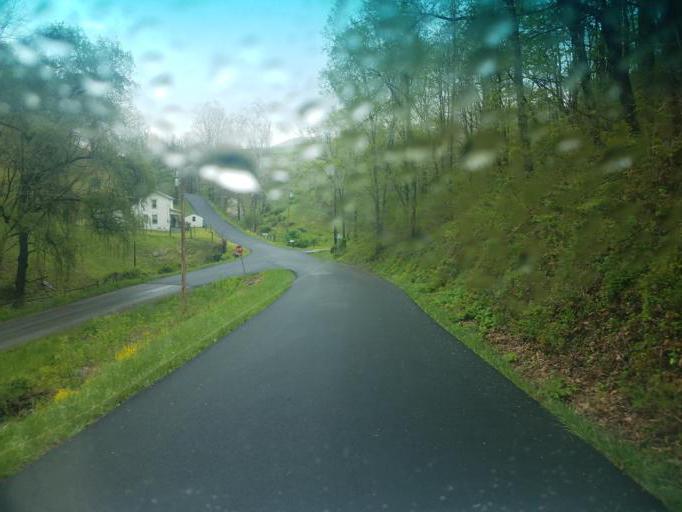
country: US
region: Virginia
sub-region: Smyth County
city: Marion
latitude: 36.9253
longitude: -81.5532
